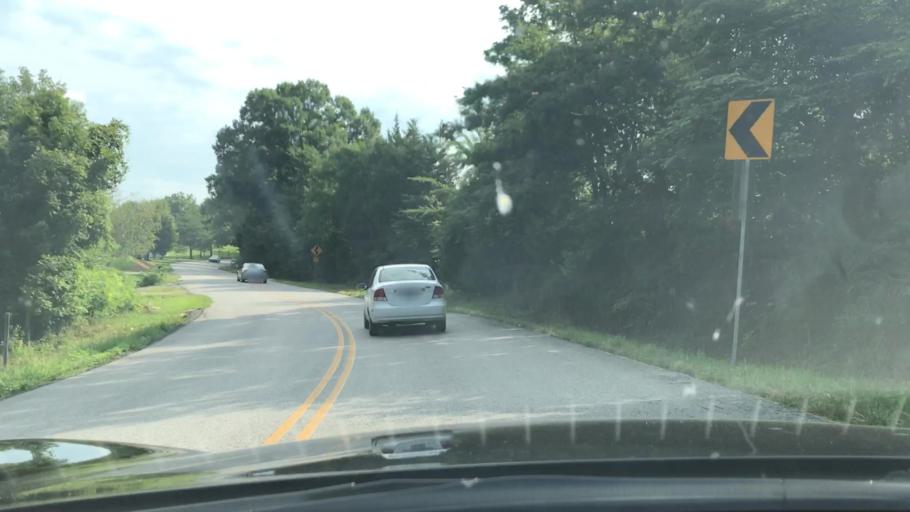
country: US
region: Kentucky
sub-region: Green County
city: Greensburg
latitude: 37.2691
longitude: -85.5327
